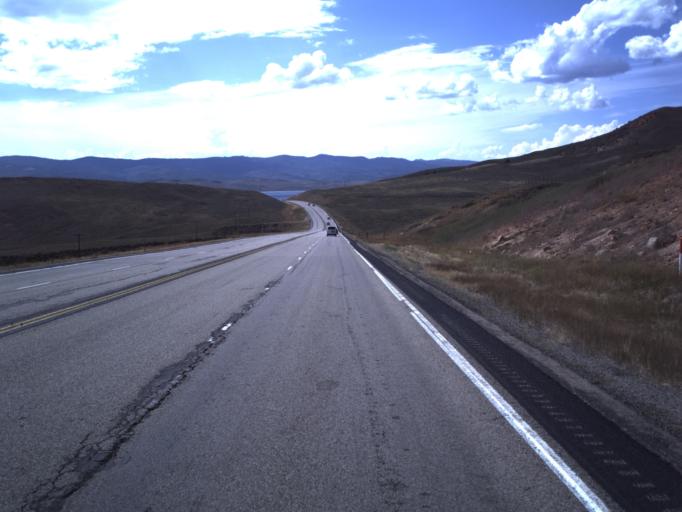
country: US
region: Utah
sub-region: Wasatch County
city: Heber
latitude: 40.1930
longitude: -111.0844
